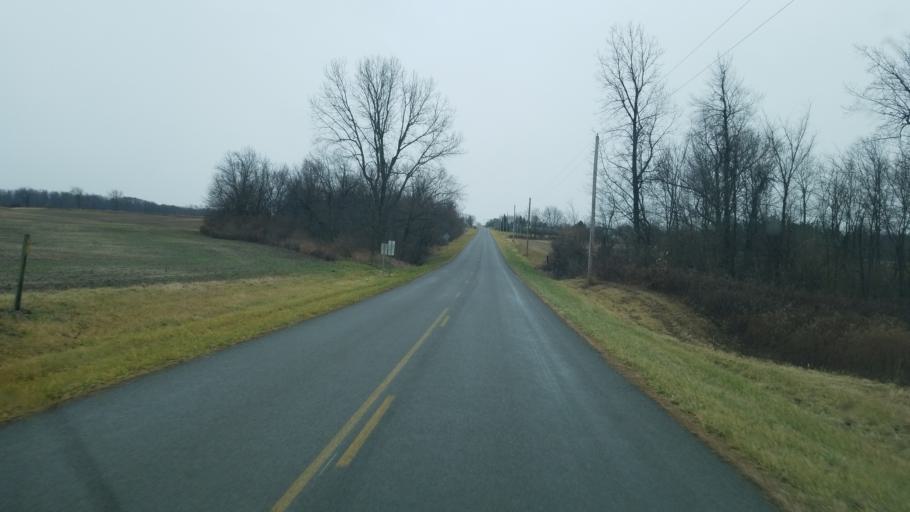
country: US
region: Ohio
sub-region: Logan County
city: Northwood
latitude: 40.4609
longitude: -83.6571
